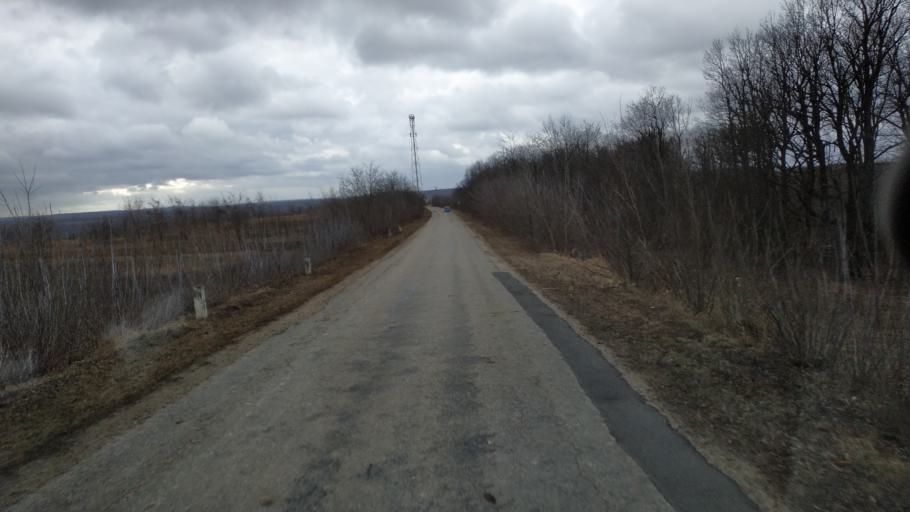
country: MD
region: Calarasi
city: Calarasi
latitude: 47.2255
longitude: 28.2319
